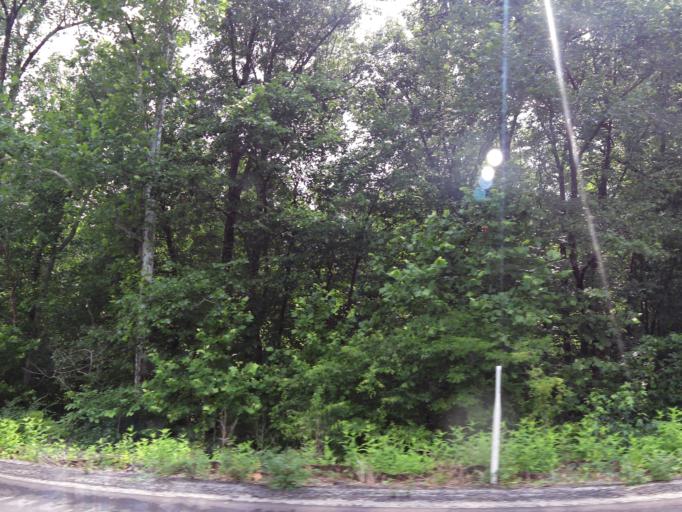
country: US
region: Kentucky
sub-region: Hopkins County
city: Madisonville
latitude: 37.3104
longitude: -87.3681
